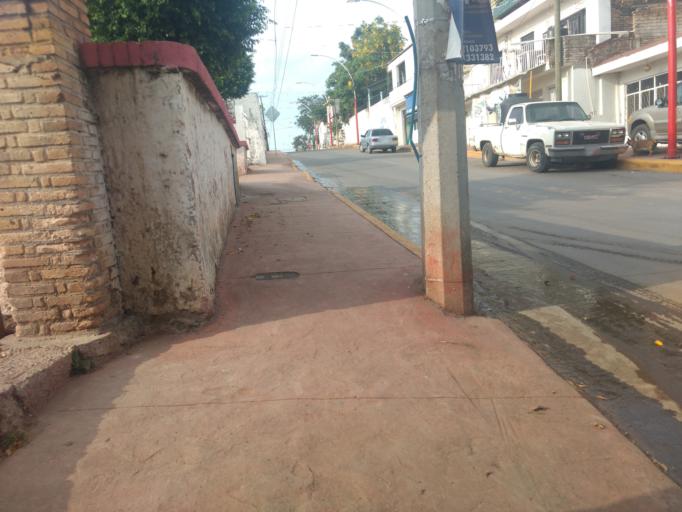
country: MX
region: Nayarit
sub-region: Tepic
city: La Corregidora
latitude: 21.4643
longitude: -104.8012
